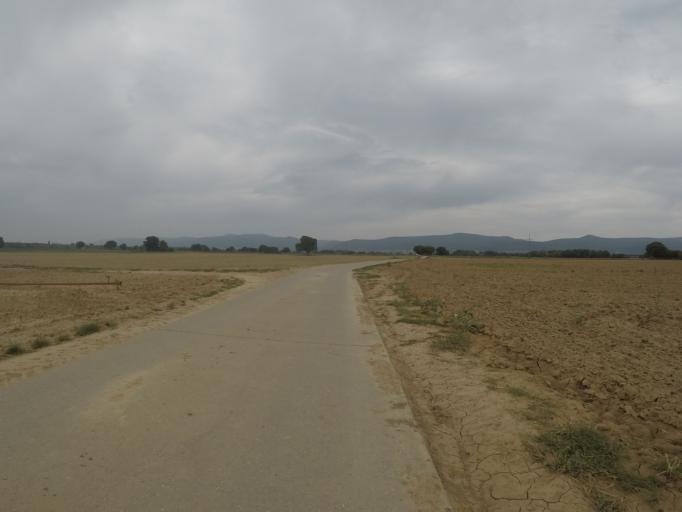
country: DE
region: Rheinland-Pfalz
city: Meckenheim
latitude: 49.3732
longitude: 8.2243
